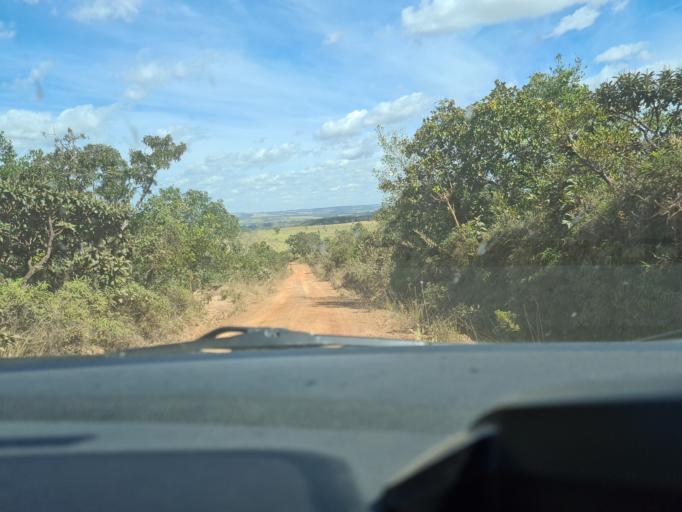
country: BR
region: Goias
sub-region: Silvania
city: Silvania
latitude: -16.5329
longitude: -48.5531
